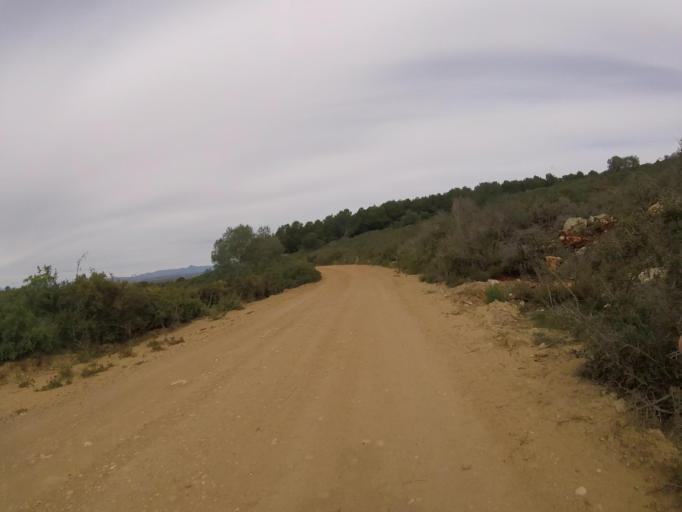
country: ES
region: Valencia
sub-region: Provincia de Castello
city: Benlloch
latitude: 40.1953
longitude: 0.0737
